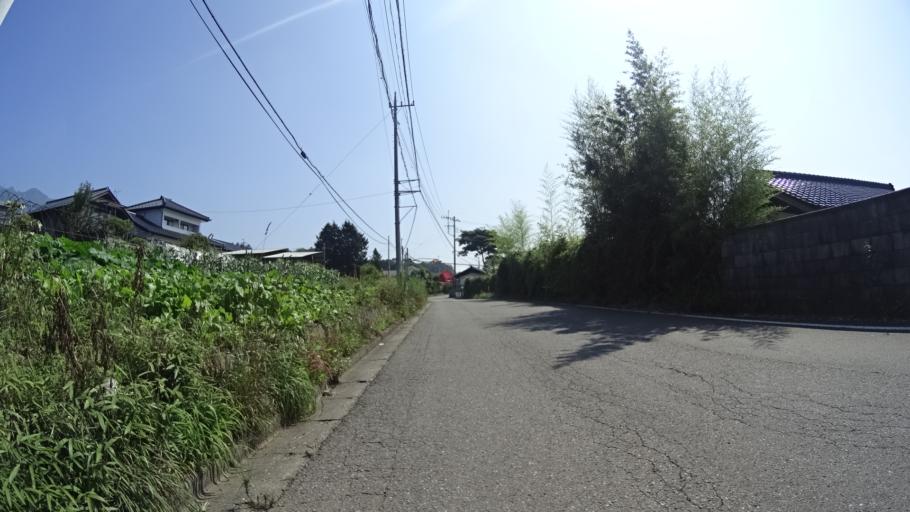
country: JP
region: Yamanashi
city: Nirasaki
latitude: 35.8775
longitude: 138.3518
